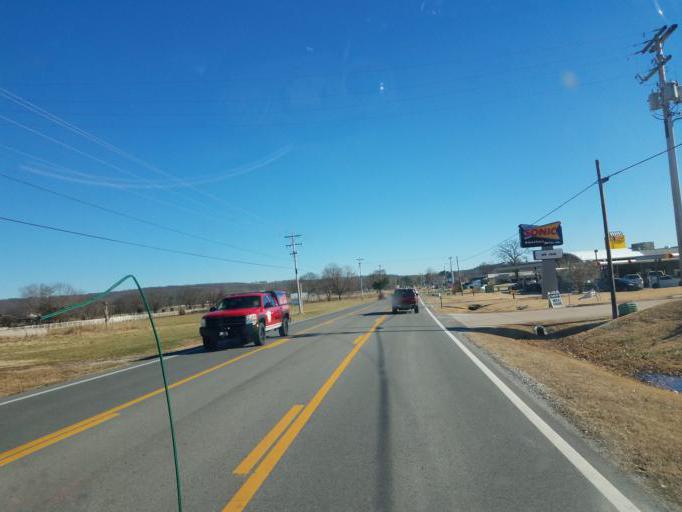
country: US
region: Arkansas
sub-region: Washington County
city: Elkins
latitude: 36.0302
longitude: -94.0298
